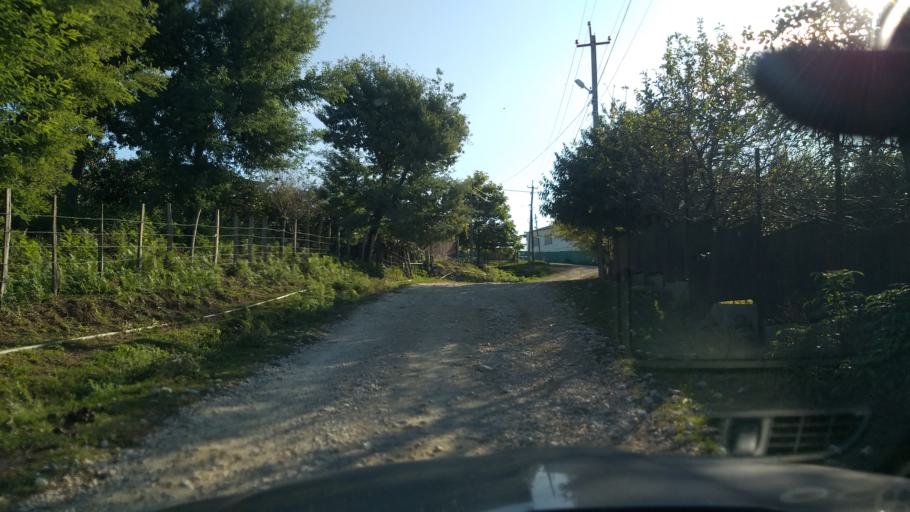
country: GE
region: Abkhazia
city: Stantsiya Novyy Afon
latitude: 43.0607
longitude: 40.8928
